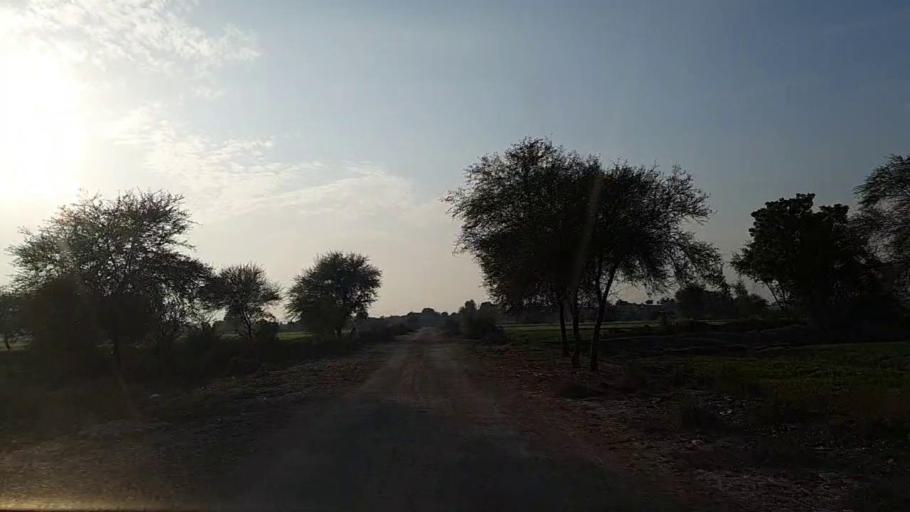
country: PK
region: Sindh
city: Jam Sahib
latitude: 26.3955
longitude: 68.5269
